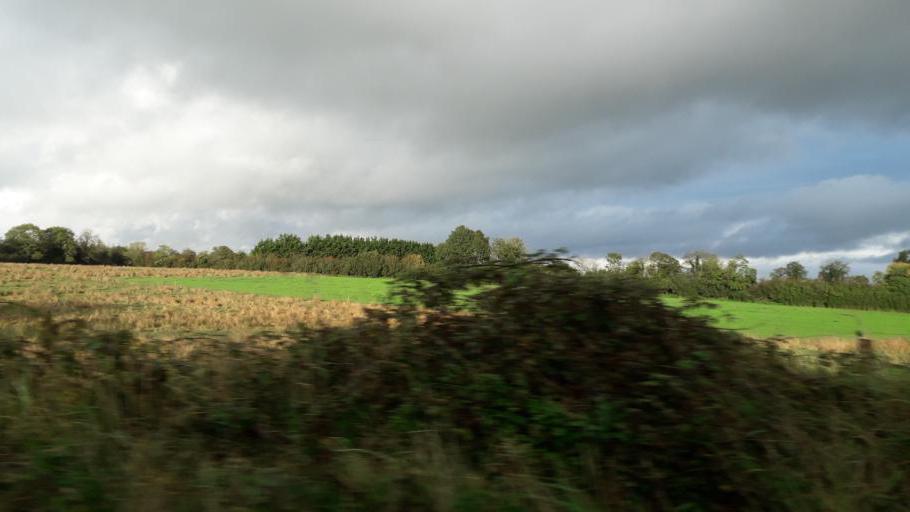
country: IE
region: Leinster
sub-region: An Longfort
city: Lanesborough
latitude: 53.7681
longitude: -8.1024
